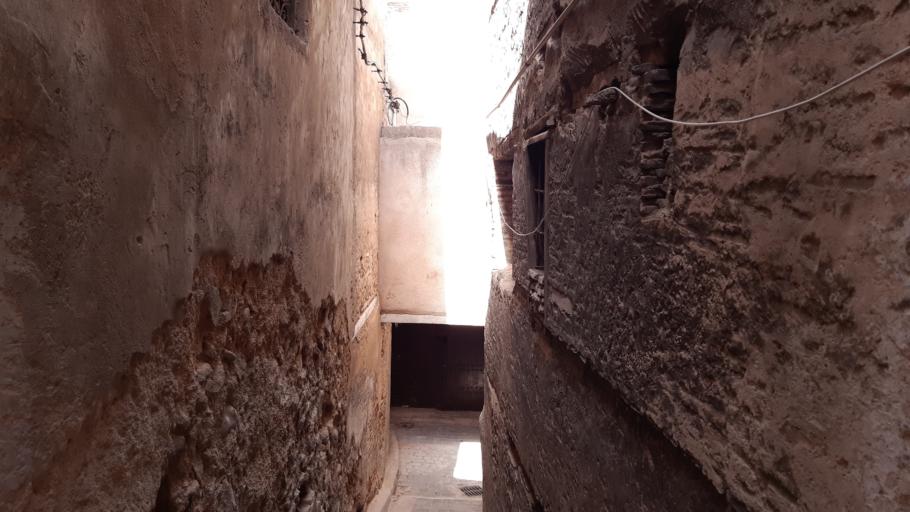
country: MA
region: Fes-Boulemane
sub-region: Fes
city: Fes
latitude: 34.0642
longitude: -4.9722
